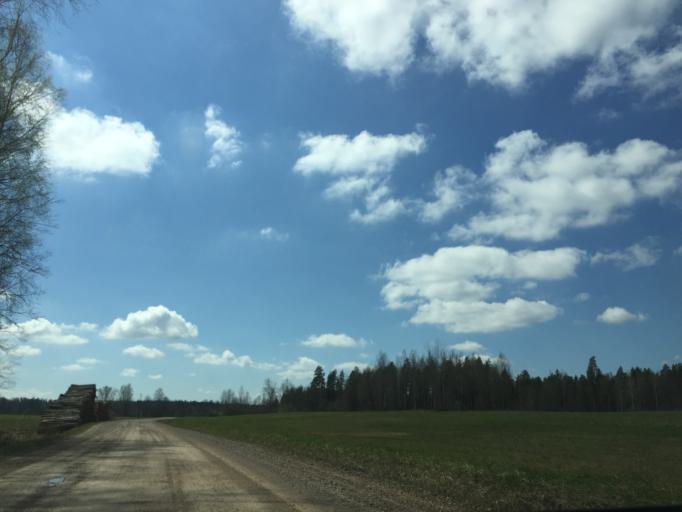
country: LV
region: Valkas Rajons
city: Valka
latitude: 57.5887
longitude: 26.0243
